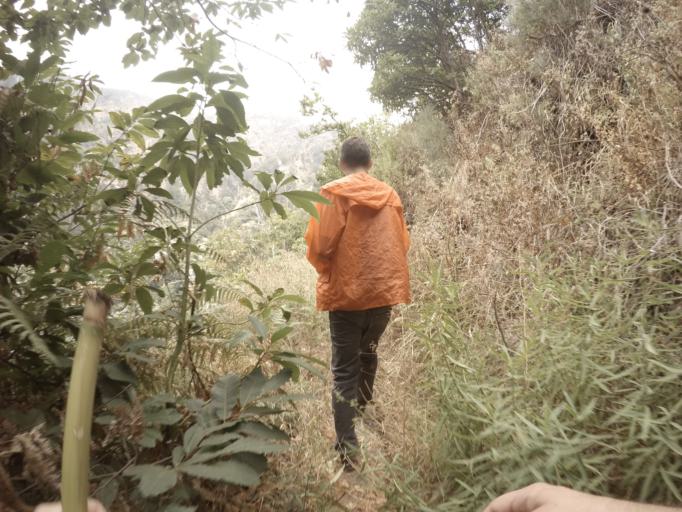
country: PT
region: Madeira
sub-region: Camara de Lobos
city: Curral das Freiras
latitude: 32.7060
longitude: -16.9688
